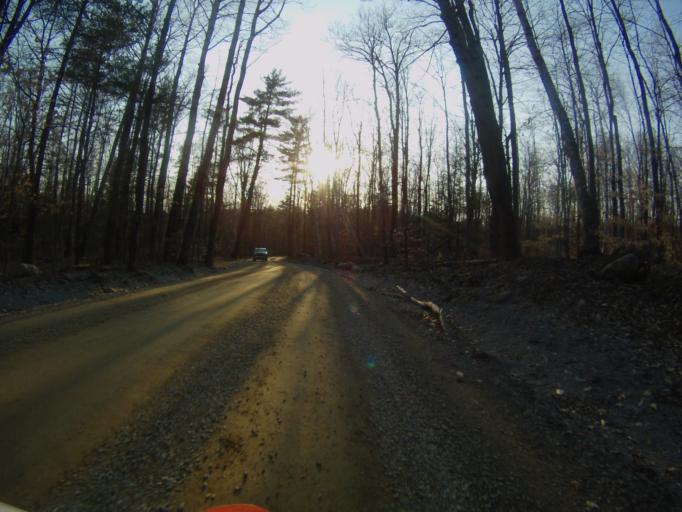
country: US
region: Vermont
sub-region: Addison County
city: Bristol
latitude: 44.0539
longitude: -73.0972
